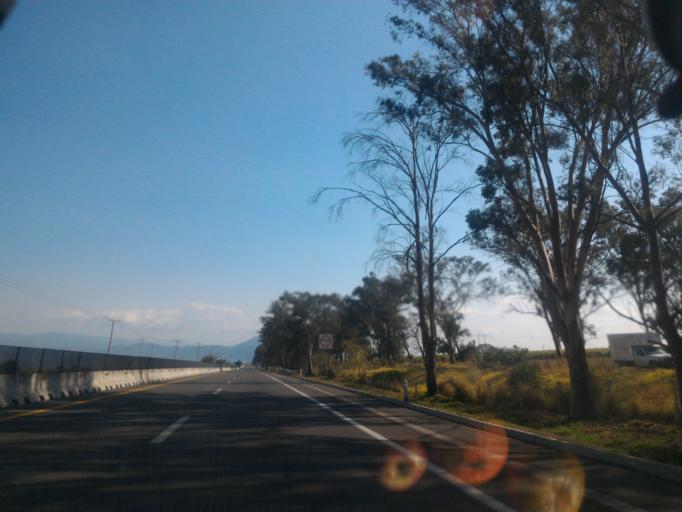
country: MX
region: Jalisco
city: Zapotiltic
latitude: 19.5874
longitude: -103.4503
